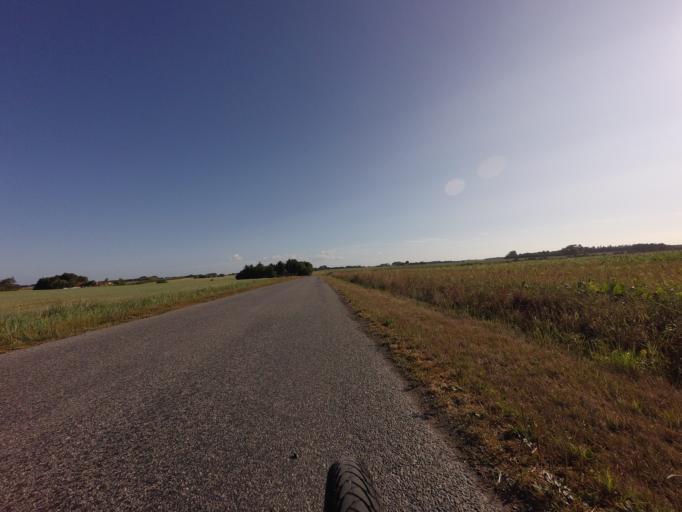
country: DK
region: North Denmark
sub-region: Hjorring Kommune
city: Vra
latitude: 57.3858
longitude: 9.9247
